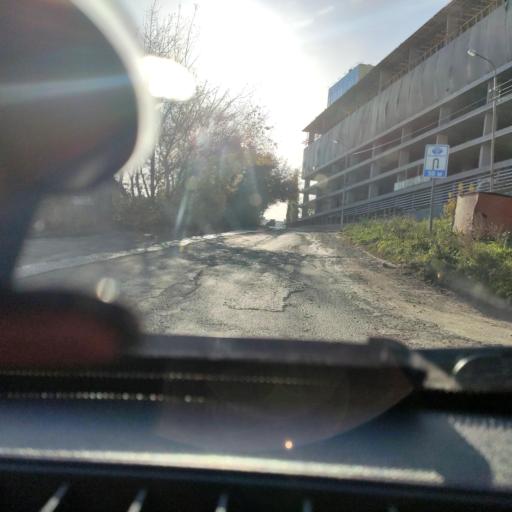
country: RU
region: Bashkortostan
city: Ufa
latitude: 54.7269
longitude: 55.9980
